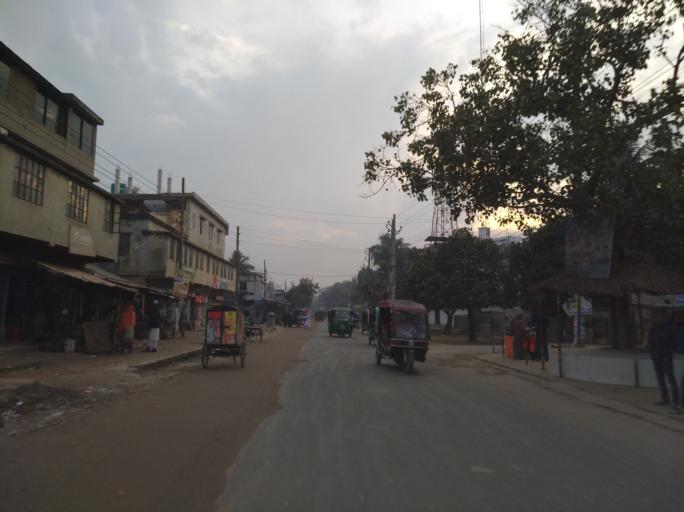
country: BD
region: Khulna
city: Khulna
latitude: 22.8479
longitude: 89.5426
